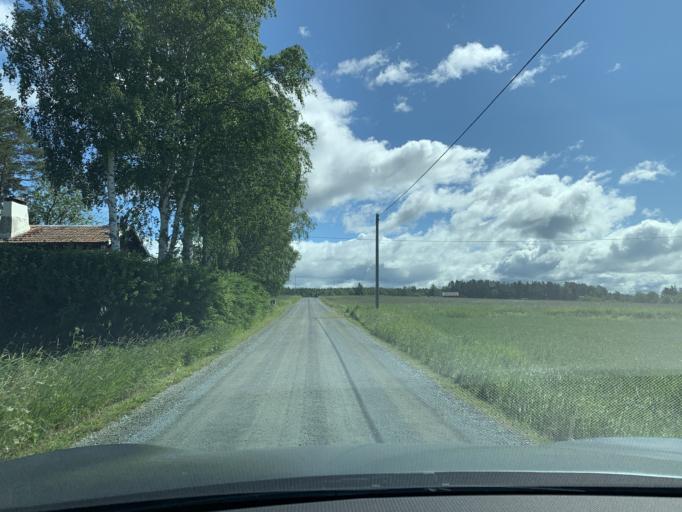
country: SE
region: Jaemtland
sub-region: Krokoms Kommun
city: Krokom
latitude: 63.1483
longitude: 14.3422
